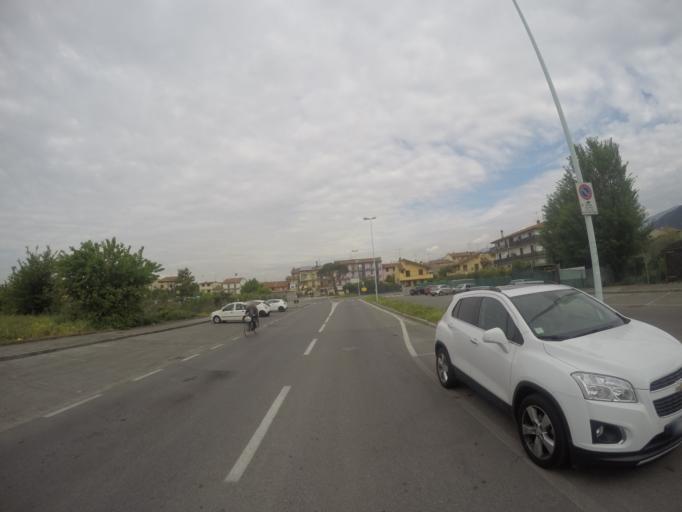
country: IT
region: Tuscany
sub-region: Provincia di Prato
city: Prato
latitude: 43.8992
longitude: 11.0703
